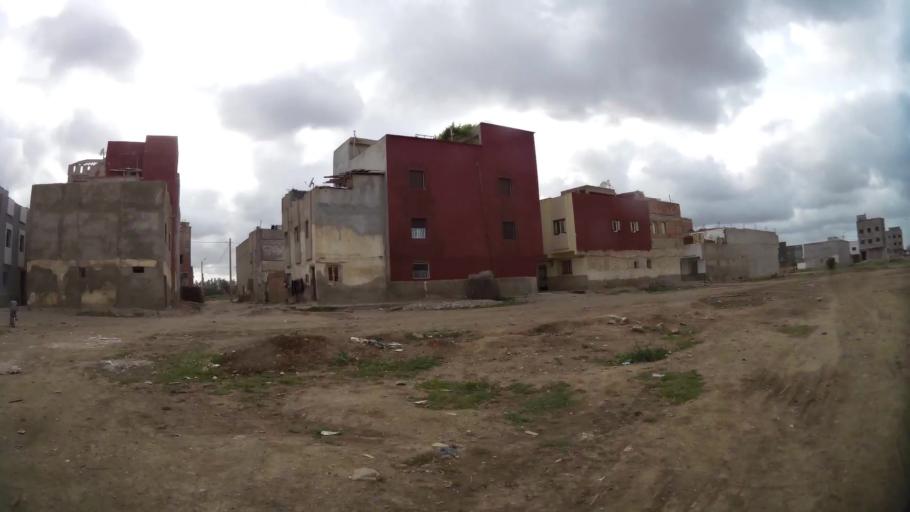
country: MA
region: Oriental
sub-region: Nador
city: Nador
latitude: 35.1574
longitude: -2.9145
